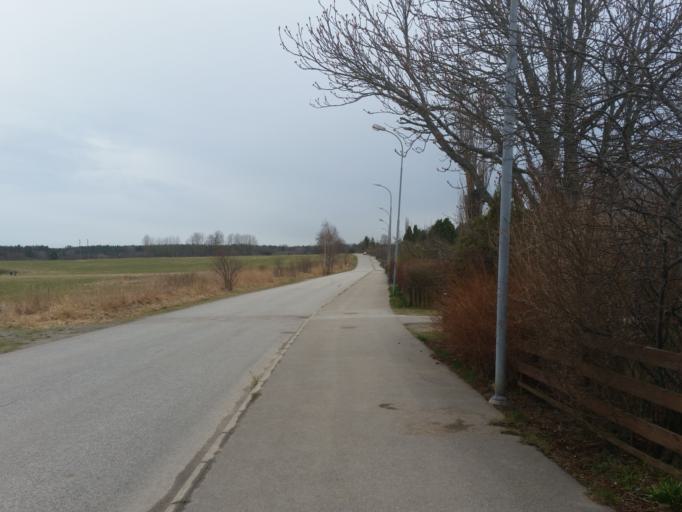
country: SE
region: Stockholm
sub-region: Sodertalje Kommun
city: Pershagen
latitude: 59.0839
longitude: 17.5689
